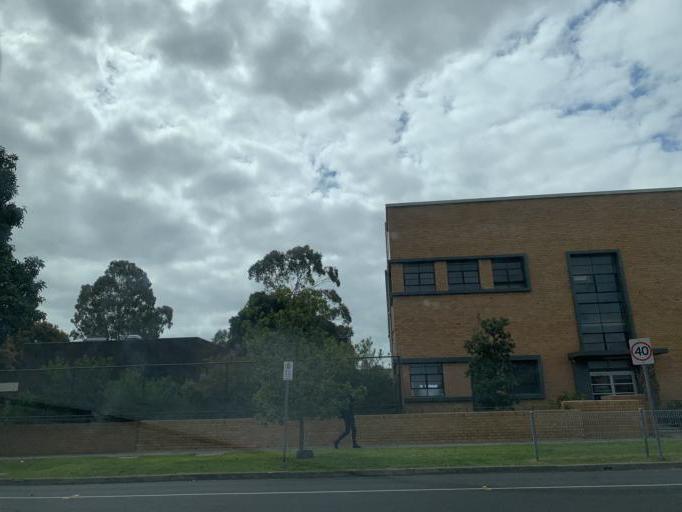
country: AU
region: Victoria
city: Thornbury
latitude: -37.7349
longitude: 144.9921
